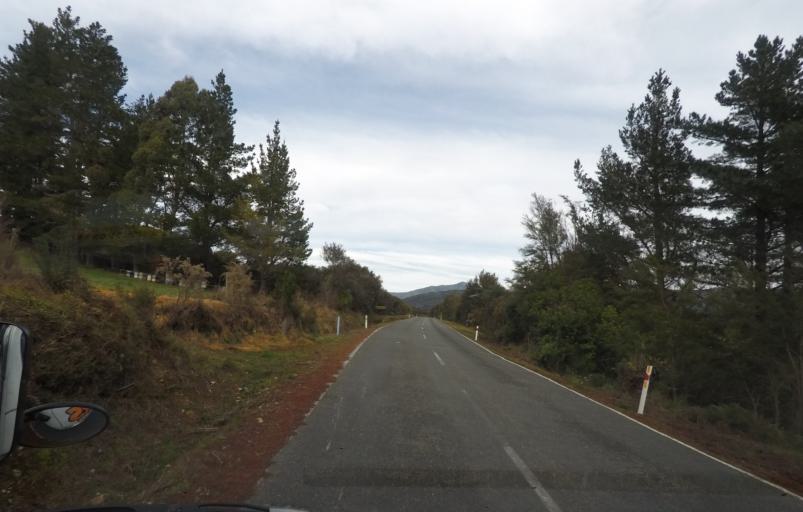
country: NZ
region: Tasman
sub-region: Tasman District
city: Takaka
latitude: -40.8425
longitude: 172.7757
